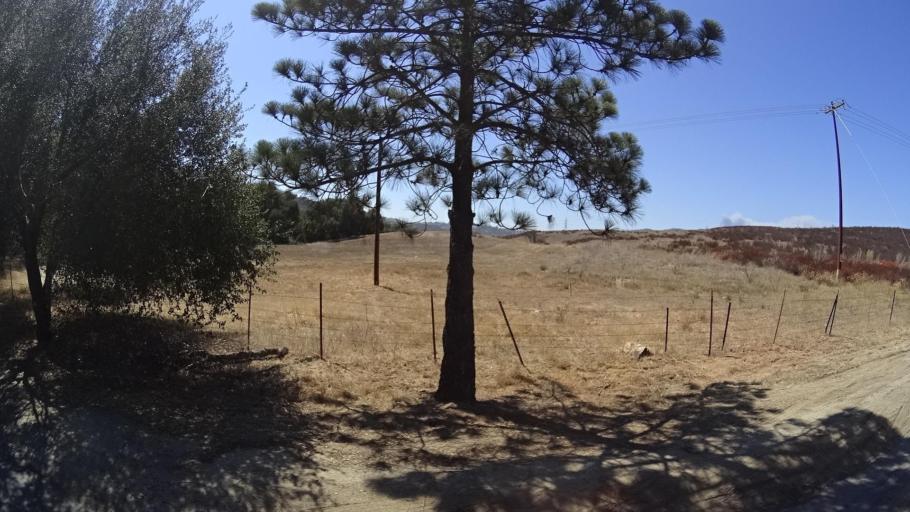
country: US
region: California
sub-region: San Diego County
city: Hidden Meadows
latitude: 33.2887
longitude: -117.0833
